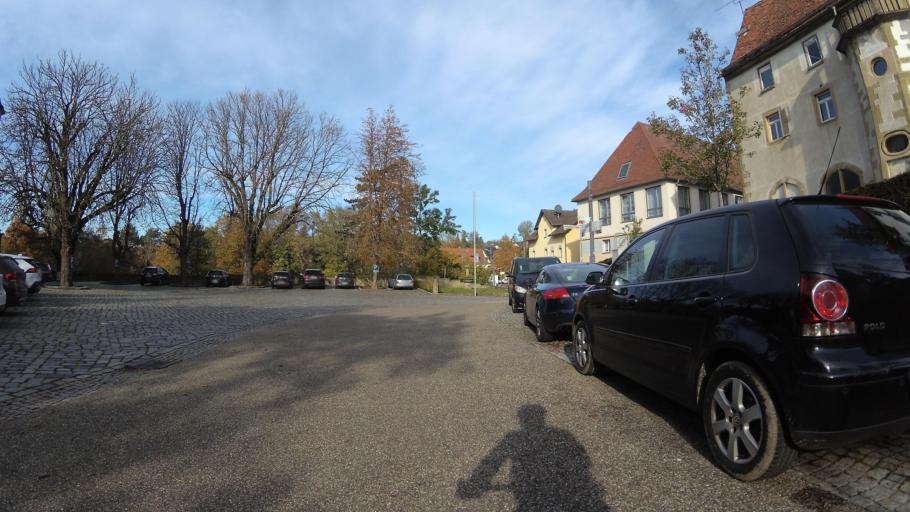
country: DE
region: Baden-Wuerttemberg
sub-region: Regierungsbezirk Stuttgart
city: Neuenstein
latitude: 49.2044
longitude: 9.5794
